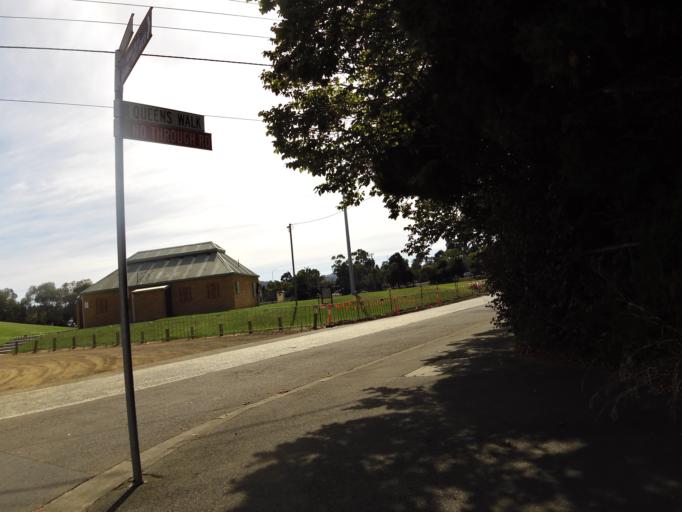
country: AU
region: Tasmania
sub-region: Hobart
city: New Town
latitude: -42.8516
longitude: 147.3115
